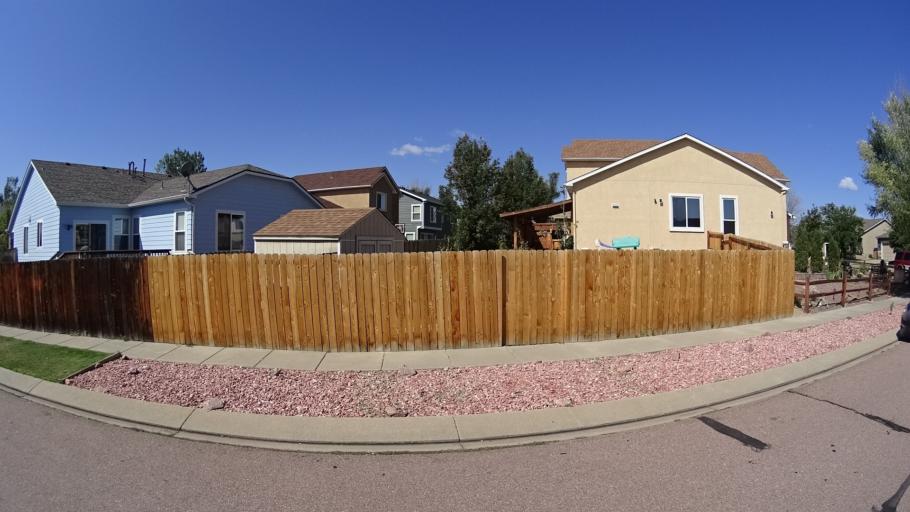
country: US
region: Colorado
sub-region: El Paso County
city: Cimarron Hills
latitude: 38.9233
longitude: -104.6971
